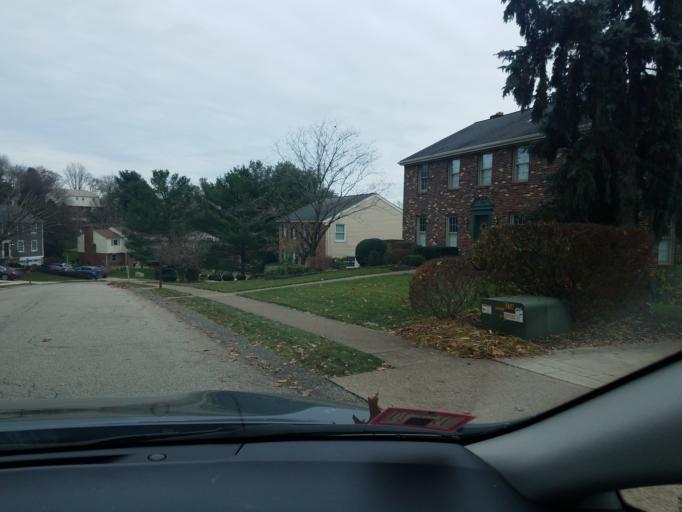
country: US
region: Pennsylvania
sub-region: Allegheny County
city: Franklin Park
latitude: 40.5546
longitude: -80.0634
